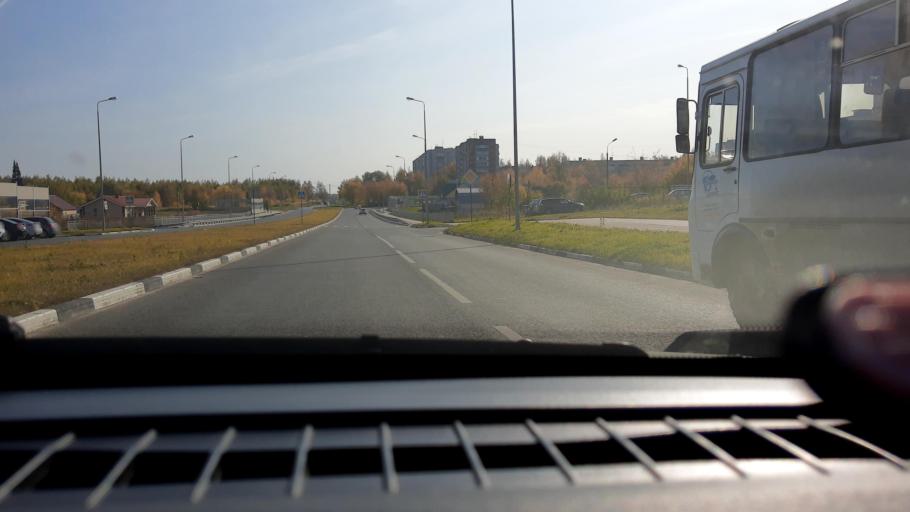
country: RU
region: Nizjnij Novgorod
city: Kstovo
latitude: 56.1548
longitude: 44.2153
